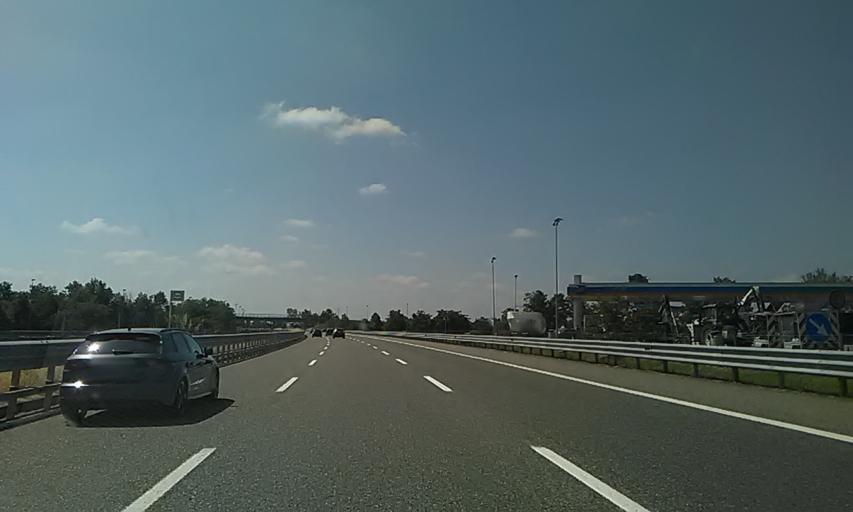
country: IT
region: Piedmont
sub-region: Provincia di Alessandria
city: Castelspina
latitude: 44.8178
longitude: 8.5944
